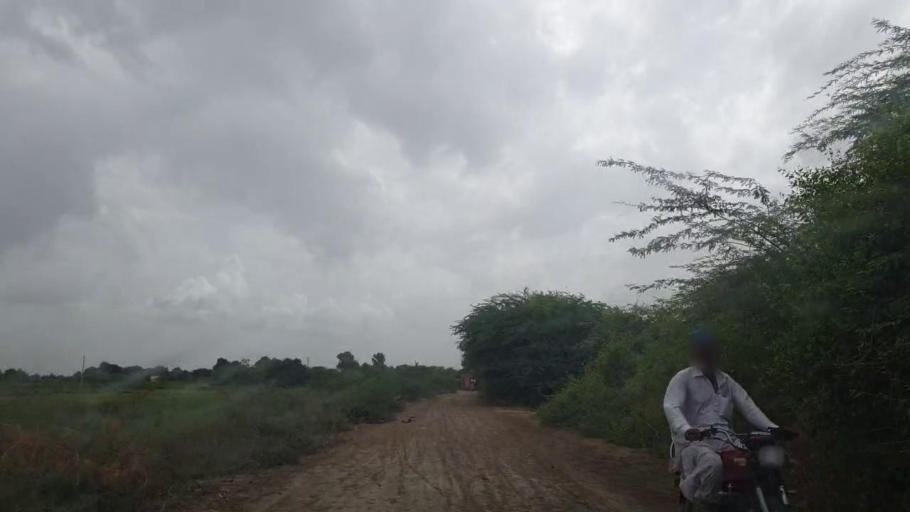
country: PK
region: Sindh
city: Naukot
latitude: 24.8800
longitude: 69.2458
